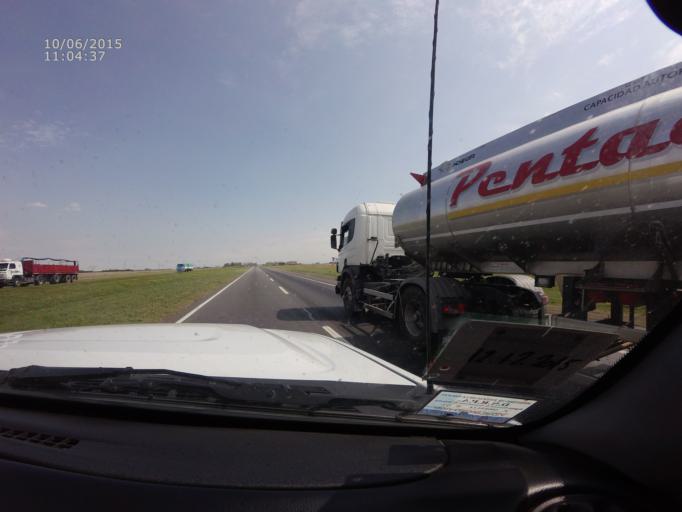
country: AR
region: Santa Fe
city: Arroyo Seco
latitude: -33.2236
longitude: -60.4655
